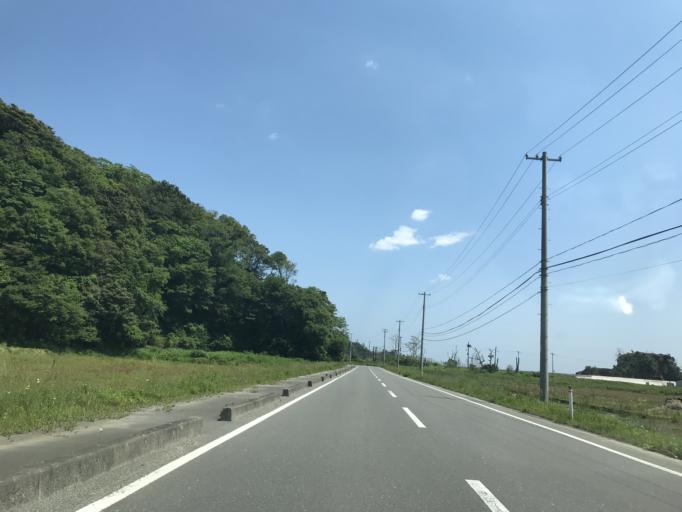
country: JP
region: Miyagi
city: Matsushima
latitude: 38.3308
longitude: 141.1614
